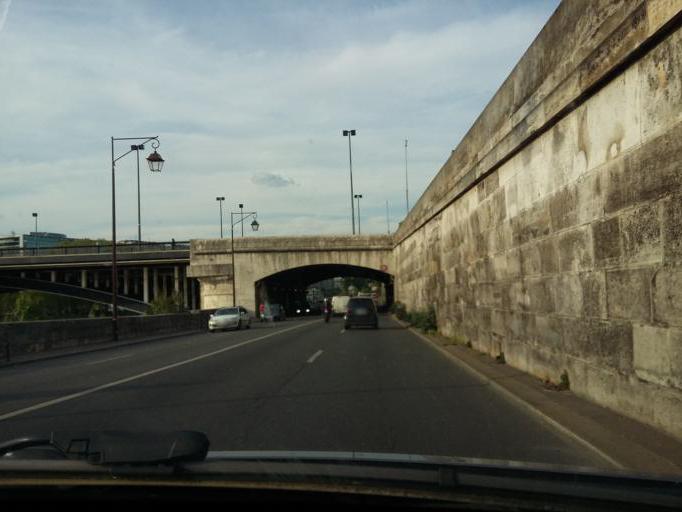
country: FR
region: Ile-de-France
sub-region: Departement des Hauts-de-Seine
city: Courbevoie
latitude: 48.8855
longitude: 2.2555
